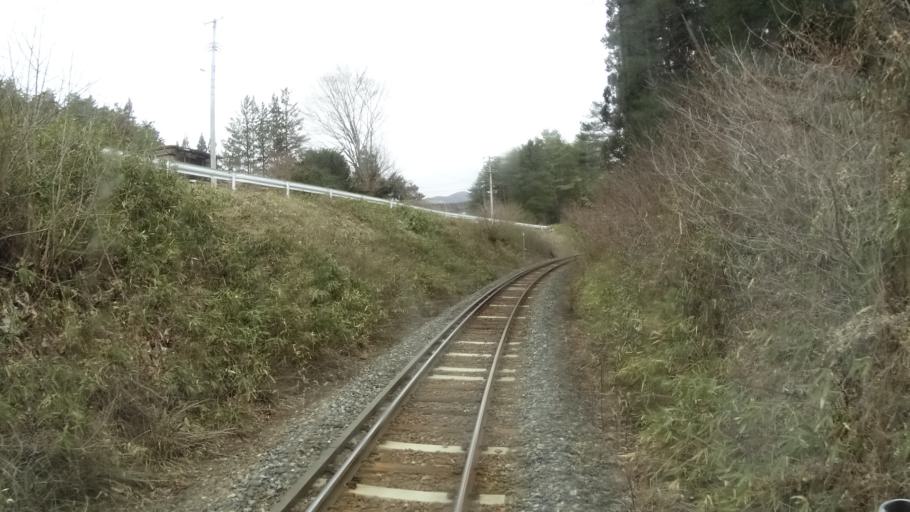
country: JP
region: Iwate
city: Tono
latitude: 39.3392
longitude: 141.3524
